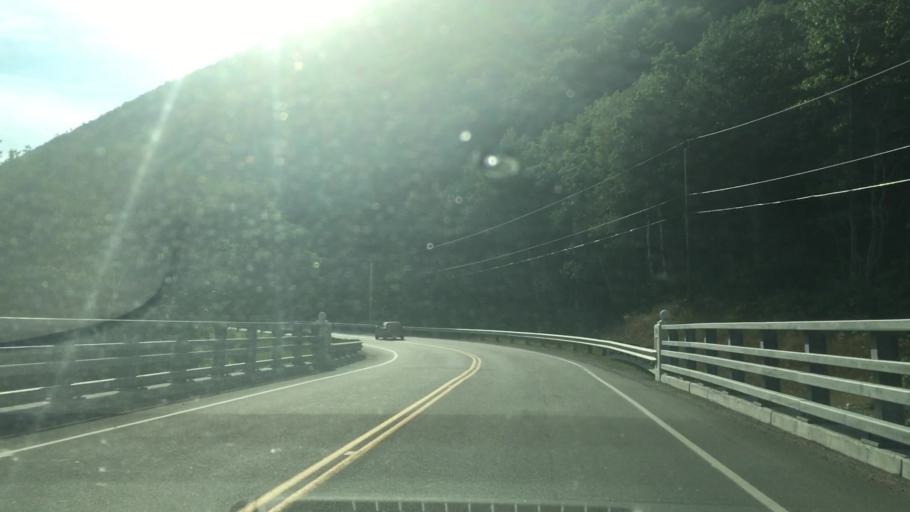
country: CA
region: Nova Scotia
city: Sydney Mines
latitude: 46.8280
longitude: -60.6189
